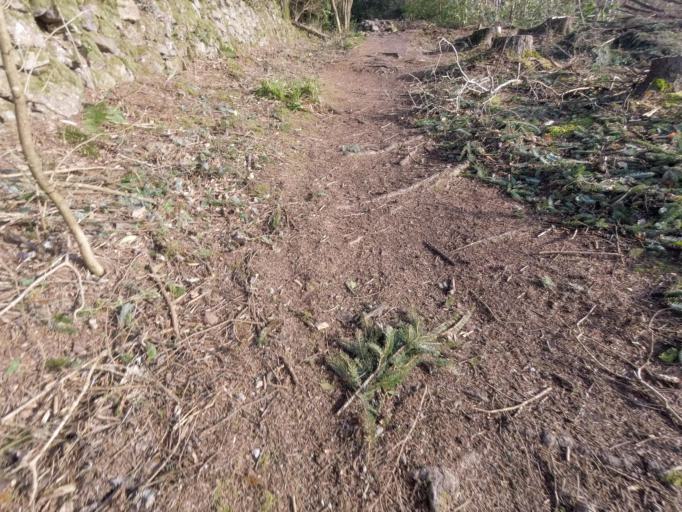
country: IE
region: Munster
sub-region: Waterford
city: Waterford
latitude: 52.2669
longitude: -7.0157
